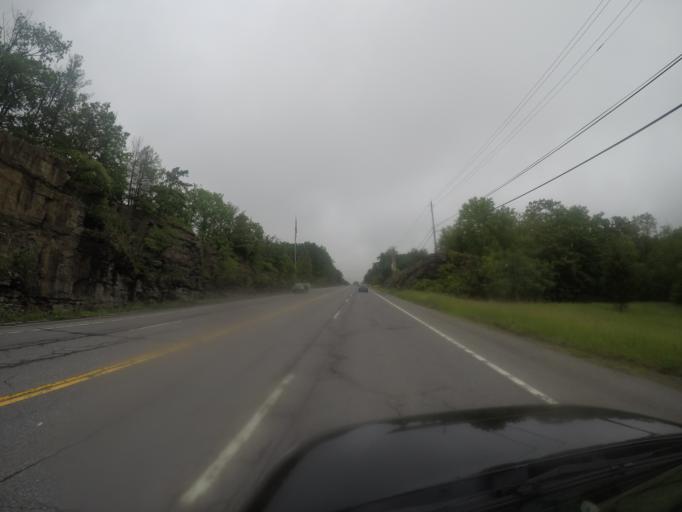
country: US
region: New York
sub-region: Ulster County
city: West Hurley
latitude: 41.9852
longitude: -74.0861
